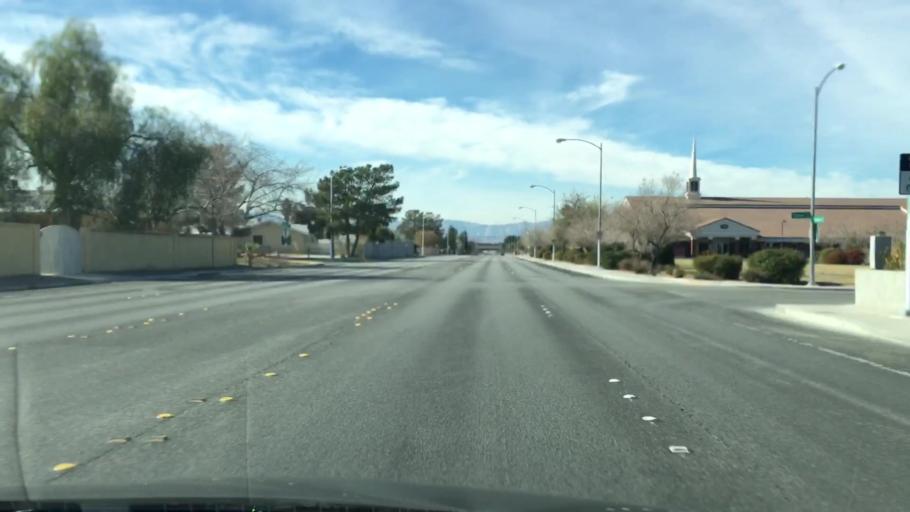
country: US
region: Nevada
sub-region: Clark County
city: Whitney
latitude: 36.0497
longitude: -115.1226
